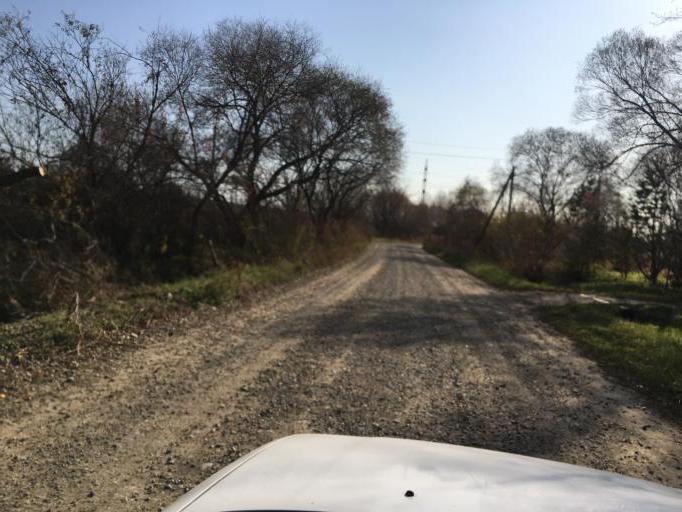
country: RU
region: Primorskiy
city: Dal'nerechensk
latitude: 45.9162
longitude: 133.7152
